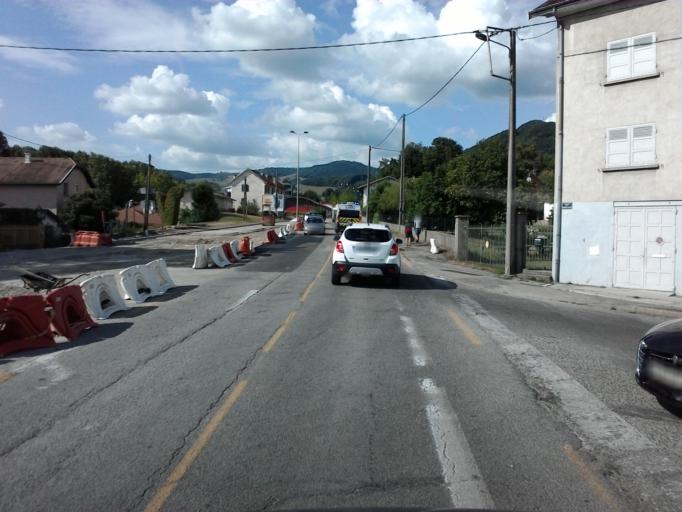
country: FR
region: Rhone-Alpes
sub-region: Departement de l'Isere
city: Voiron
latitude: 45.3741
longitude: 5.5803
